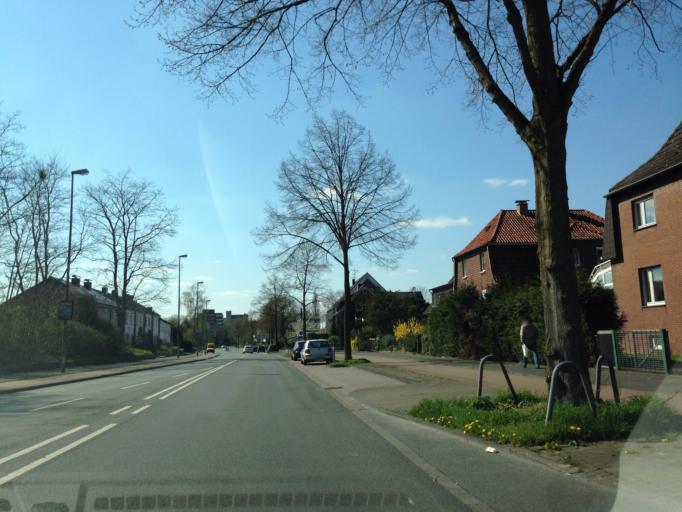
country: DE
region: North Rhine-Westphalia
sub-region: Regierungsbezirk Munster
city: Muenster
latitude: 51.9936
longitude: 7.6111
